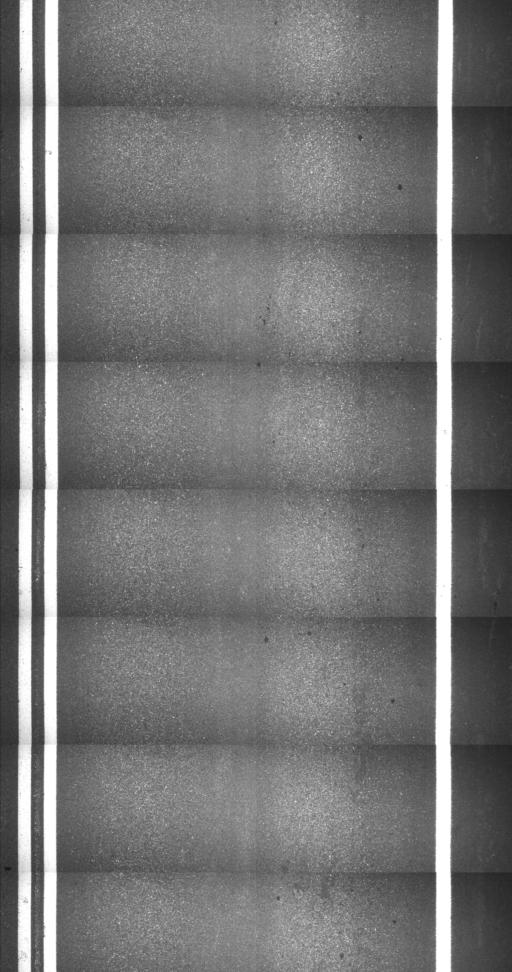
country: US
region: Vermont
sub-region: Orange County
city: Randolph
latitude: 43.9669
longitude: -72.7439
